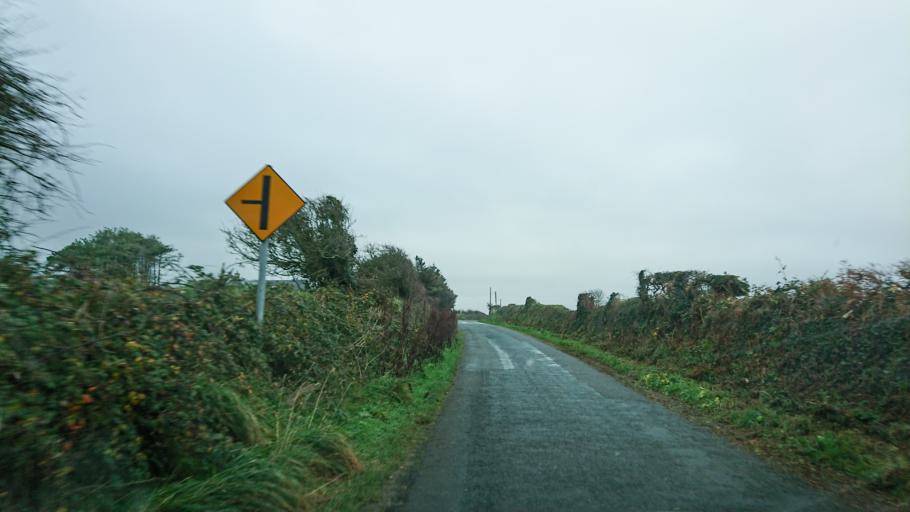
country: IE
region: Munster
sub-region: Waterford
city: Tra Mhor
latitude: 52.1404
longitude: -7.2234
